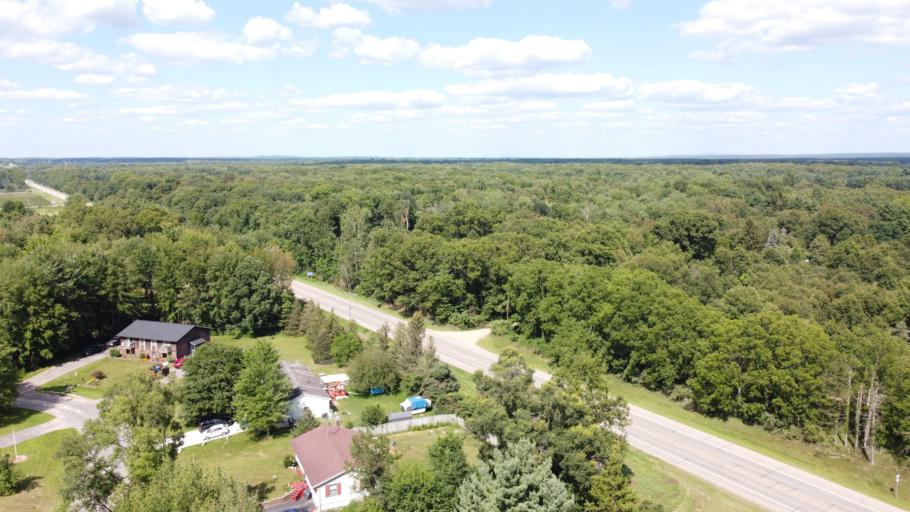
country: US
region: Michigan
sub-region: Van Buren County
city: Paw Paw
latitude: 42.2526
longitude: -85.8798
